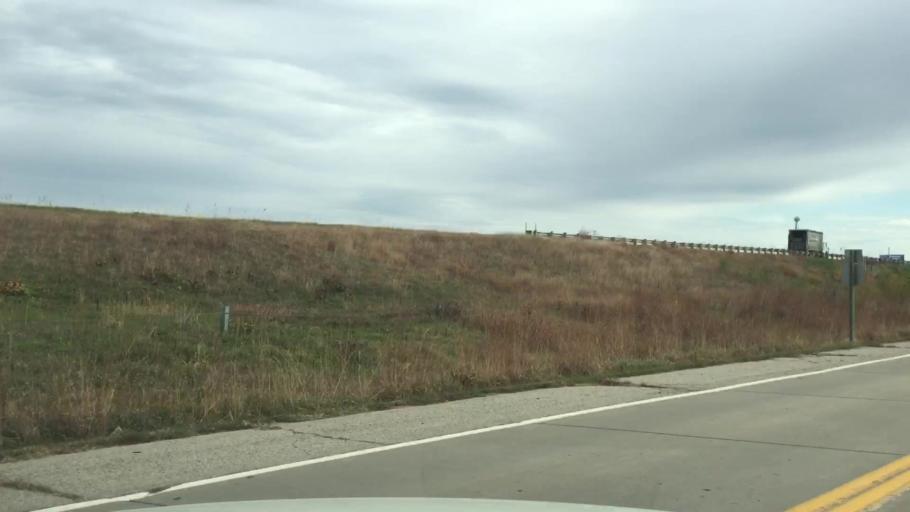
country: US
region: Kansas
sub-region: Shawnee County
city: Topeka
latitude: 39.0903
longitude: -95.7136
